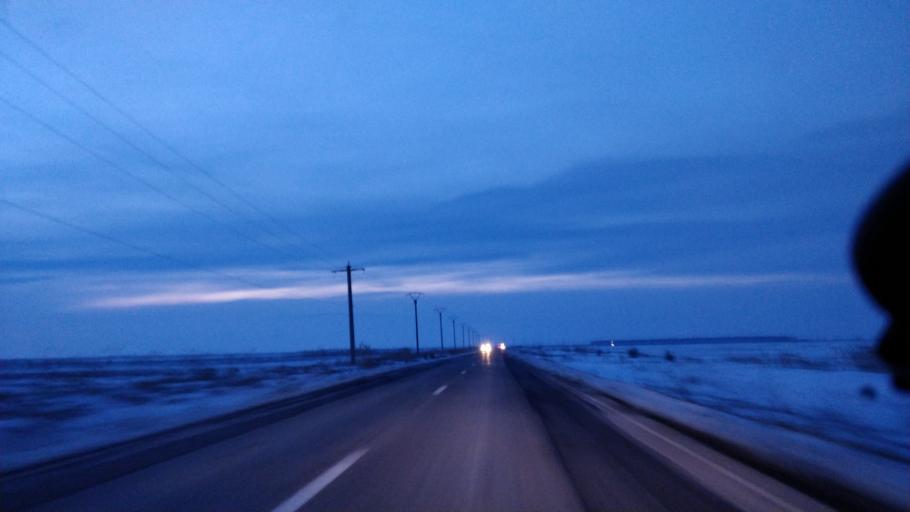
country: RO
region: Galati
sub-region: Comuna Liesti
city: Liesti
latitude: 45.5931
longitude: 27.4760
